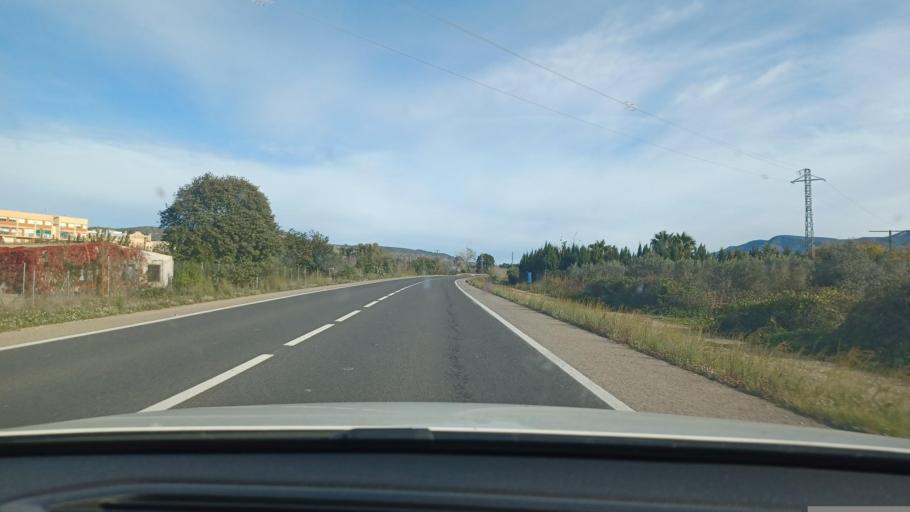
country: ES
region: Catalonia
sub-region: Provincia de Tarragona
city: Ulldecona
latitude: 40.5946
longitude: 0.4502
